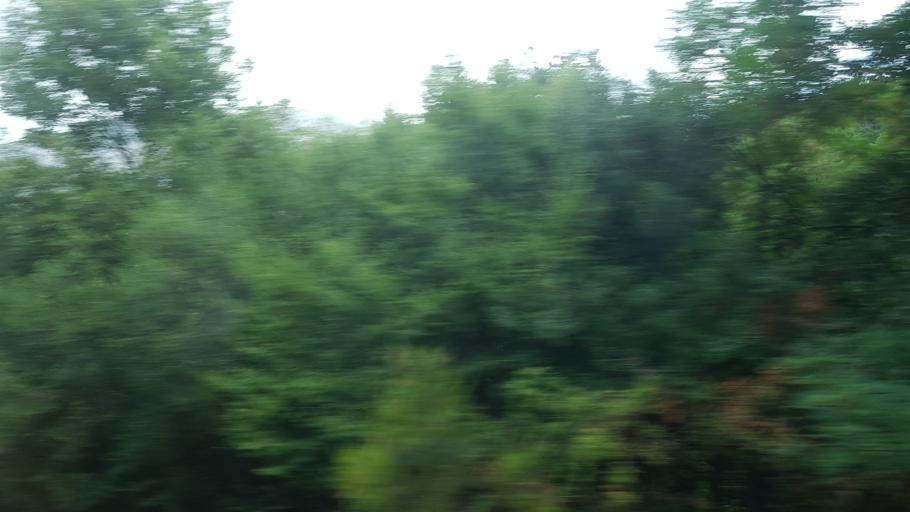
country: AL
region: Vlore
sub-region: Rrethi i Sarandes
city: Dhiver
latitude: 39.9133
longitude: 20.1891
